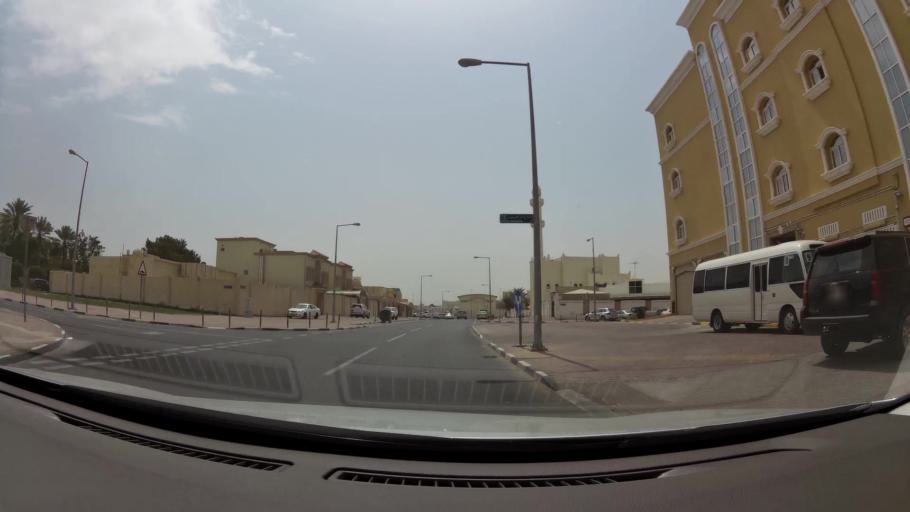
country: QA
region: Baladiyat ar Rayyan
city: Ar Rayyan
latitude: 25.3156
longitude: 51.4750
